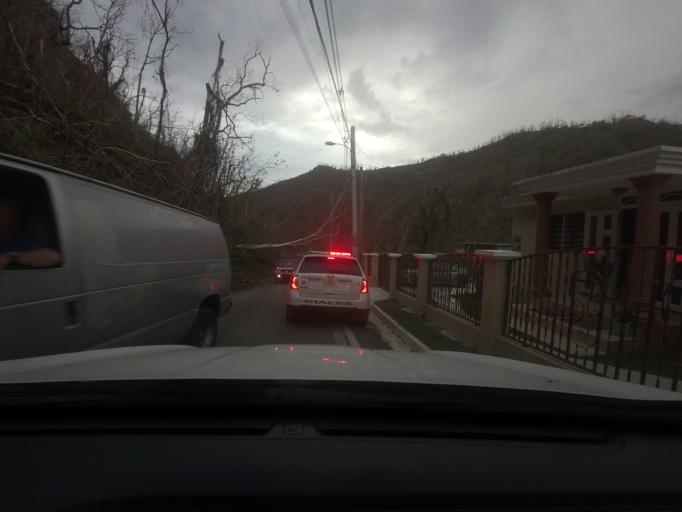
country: PR
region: Ciales
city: Ciales
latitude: 18.2898
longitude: -66.4867
